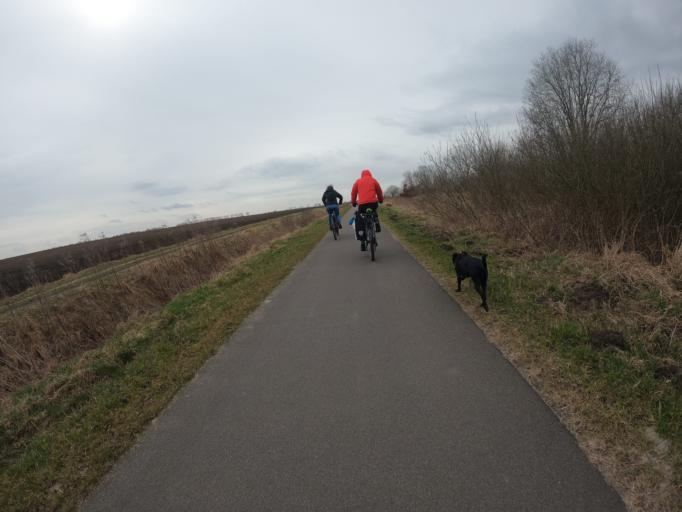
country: PL
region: West Pomeranian Voivodeship
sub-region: Powiat gryficki
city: Mrzezyno
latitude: 54.1105
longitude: 15.2960
